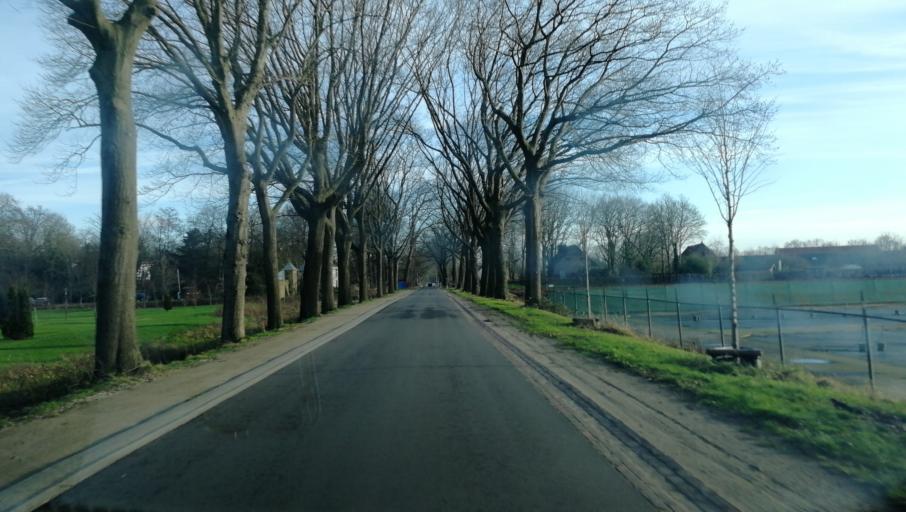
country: NL
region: Limburg
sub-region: Gemeente Venlo
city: Tegelen
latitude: 51.3433
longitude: 6.1082
